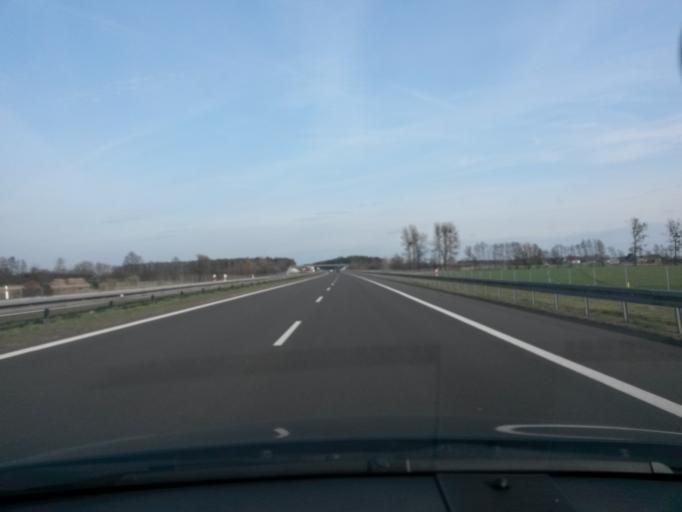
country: PL
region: Greater Poland Voivodeship
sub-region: Powiat slupecki
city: Strzalkowo
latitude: 52.2672
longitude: 17.7339
